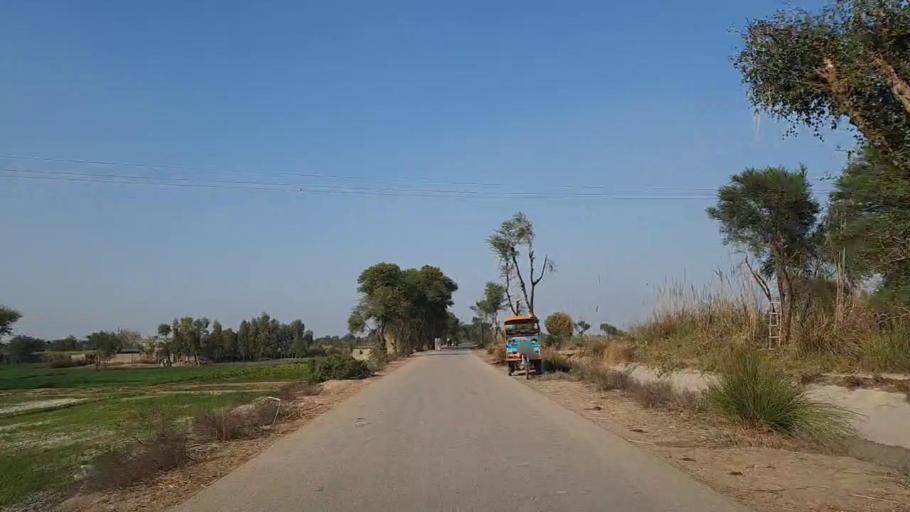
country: PK
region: Sindh
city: Daur
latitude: 26.4141
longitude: 68.2593
